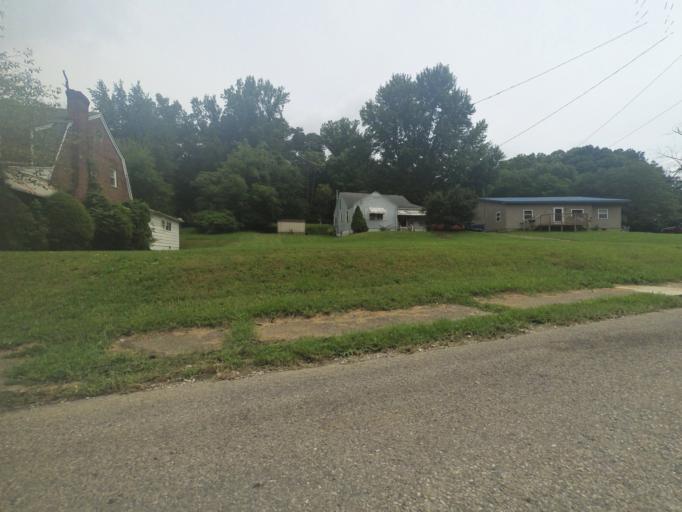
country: US
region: West Virginia
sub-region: Cabell County
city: Huntington
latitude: 38.4147
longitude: -82.4079
